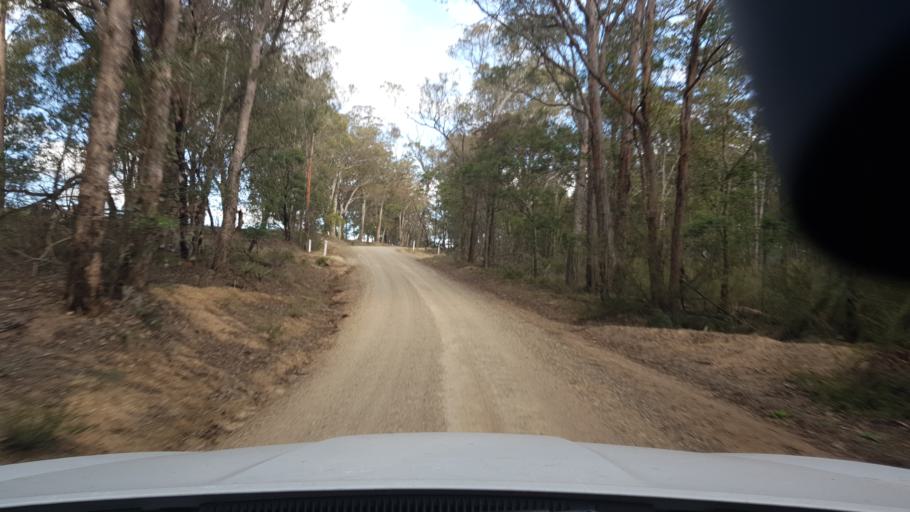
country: AU
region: Victoria
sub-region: East Gippsland
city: Bairnsdale
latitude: -37.7690
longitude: 147.5679
